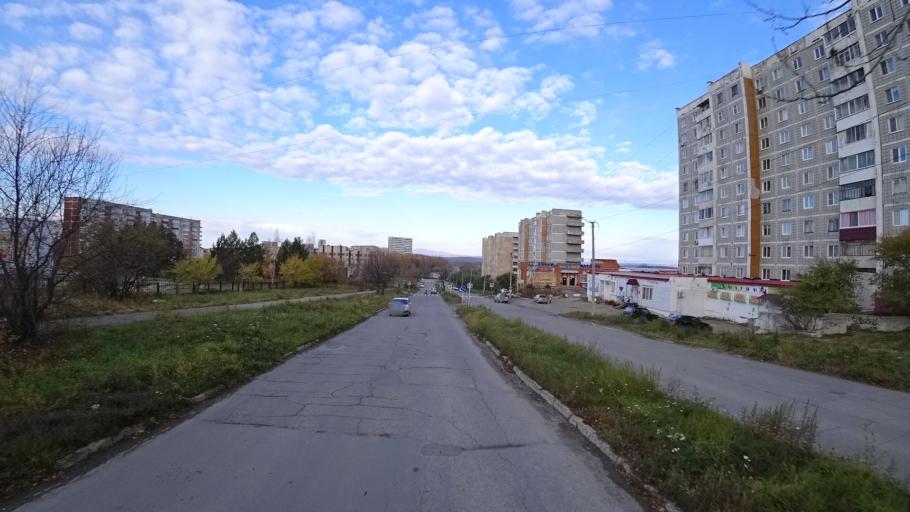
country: RU
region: Khabarovsk Krai
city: Amursk
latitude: 50.2428
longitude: 136.9187
